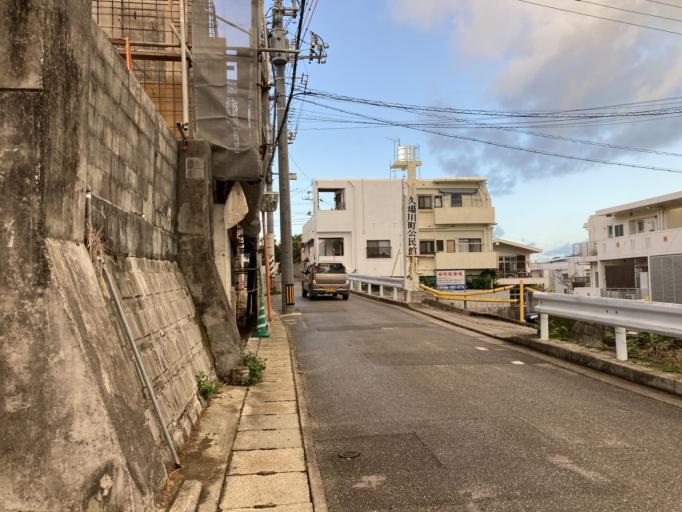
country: JP
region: Okinawa
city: Naha-shi
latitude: 26.2232
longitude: 127.7237
